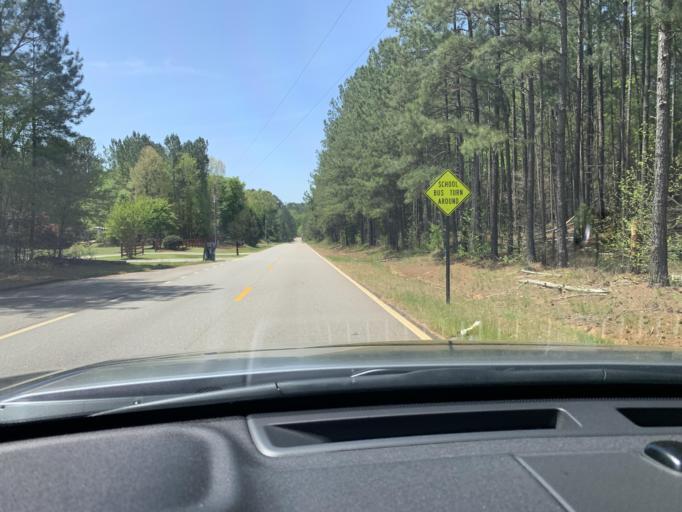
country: US
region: Georgia
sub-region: Oconee County
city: Bogart
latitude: 33.8579
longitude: -83.5709
